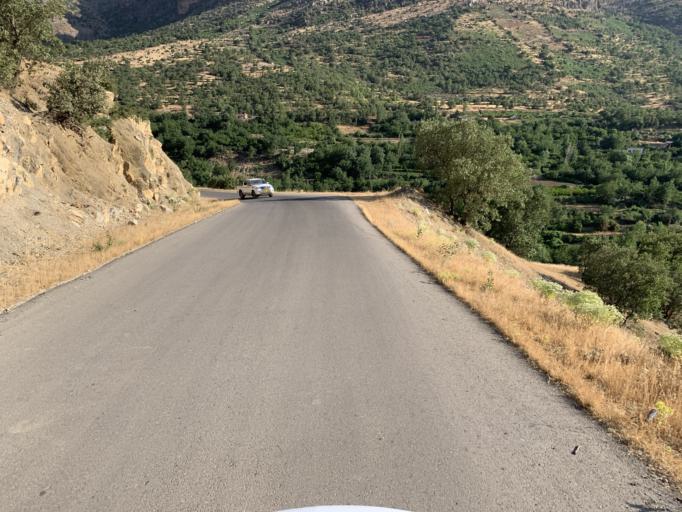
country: IQ
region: As Sulaymaniyah
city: Qeladize
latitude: 35.9934
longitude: 45.1951
